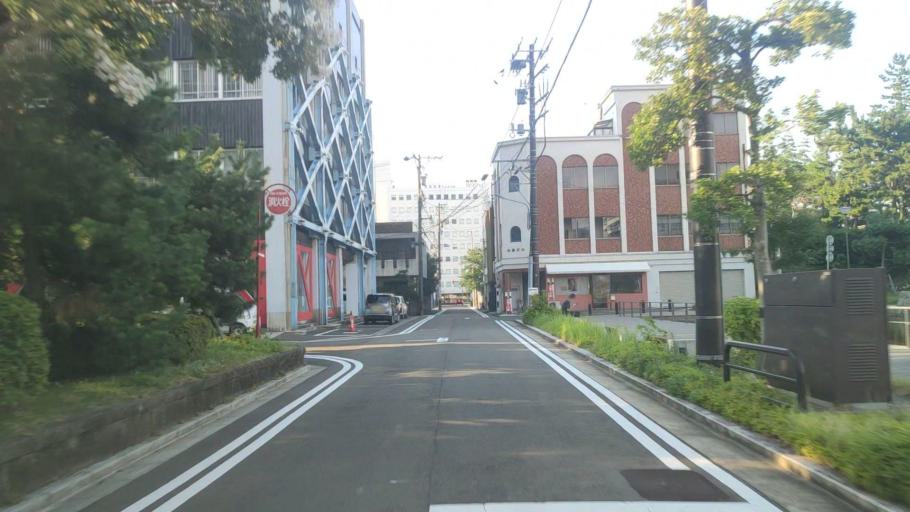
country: JP
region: Fukui
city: Fukui-shi
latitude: 36.0655
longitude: 136.2188
